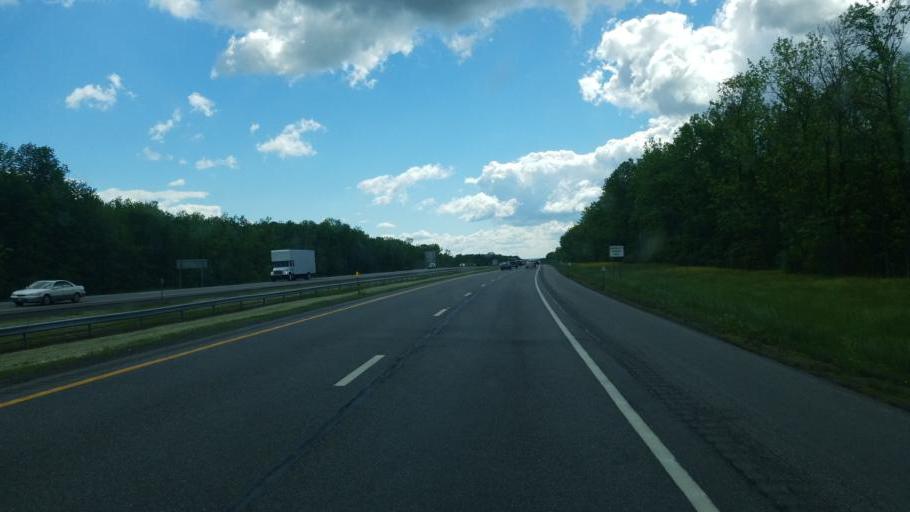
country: US
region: New York
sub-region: Madison County
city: Canastota
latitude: 43.0939
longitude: -75.8019
